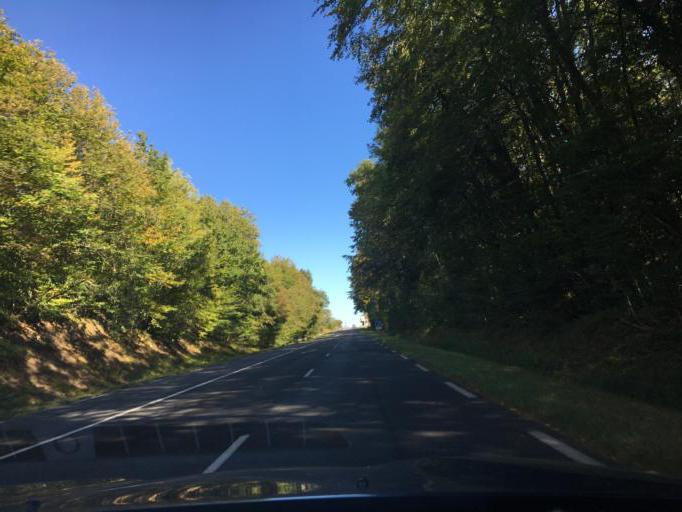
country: FR
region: Centre
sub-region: Departement d'Indre-et-Loire
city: Azay-le-Rideau
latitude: 47.2461
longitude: 0.4401
